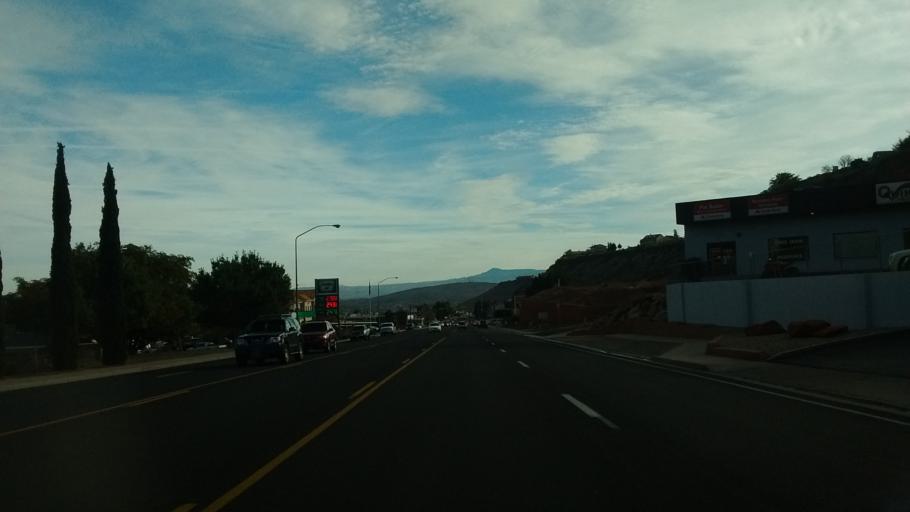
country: US
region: Utah
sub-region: Washington County
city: Saint George
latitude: 37.1158
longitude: -113.5965
